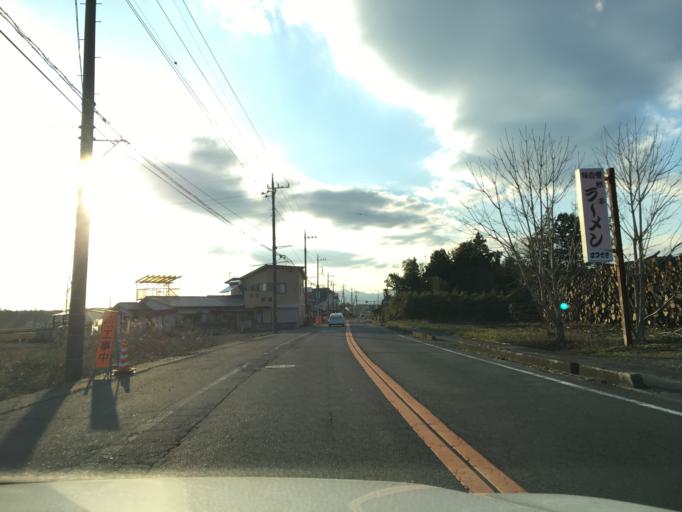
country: JP
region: Tochigi
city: Otawara
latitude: 36.8573
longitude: 140.1069
